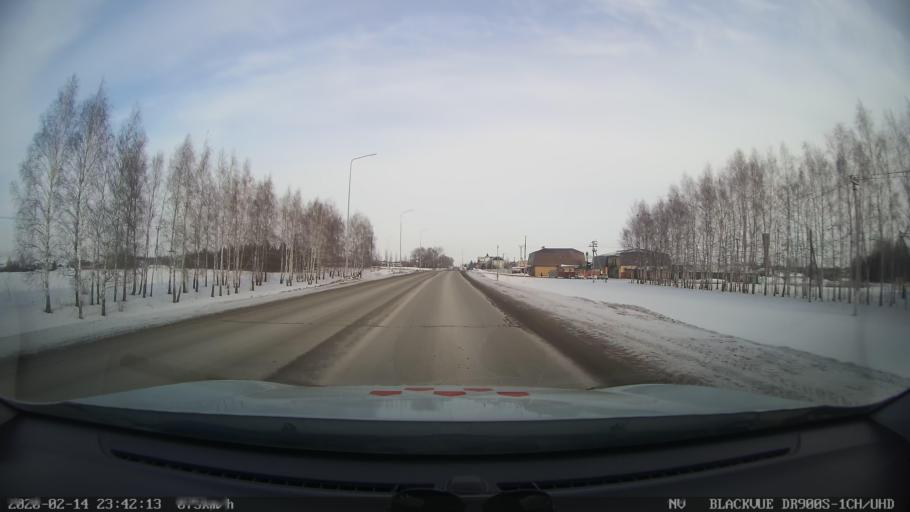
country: RU
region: Tatarstan
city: Kuybyshevskiy Zaton
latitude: 55.1897
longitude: 49.2463
